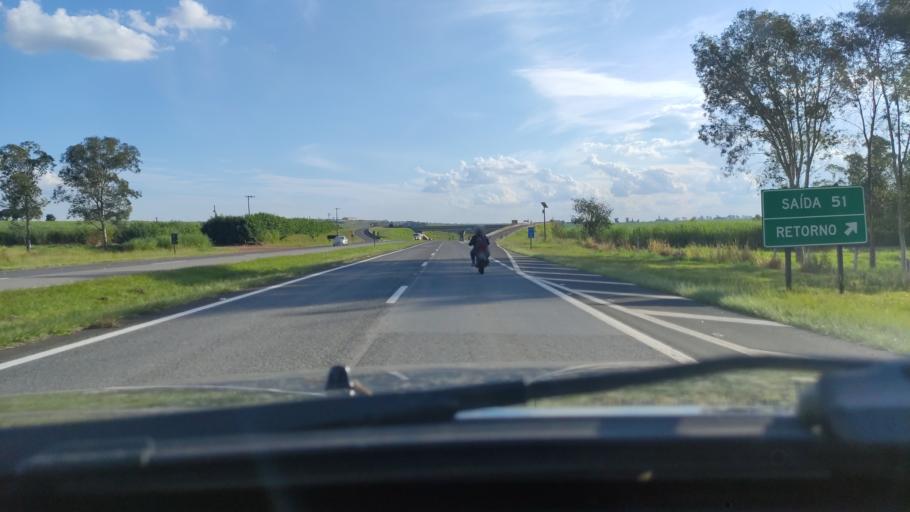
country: BR
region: Sao Paulo
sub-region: Mogi-Mirim
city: Mogi Mirim
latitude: -22.4539
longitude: -46.8939
